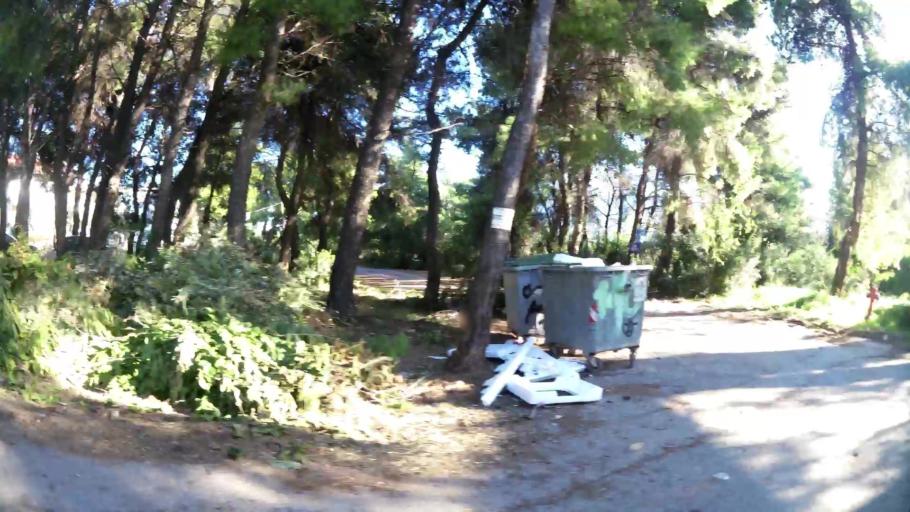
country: GR
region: Attica
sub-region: Nomarchia Anatolikis Attikis
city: Anoixi
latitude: 38.1363
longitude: 23.8492
